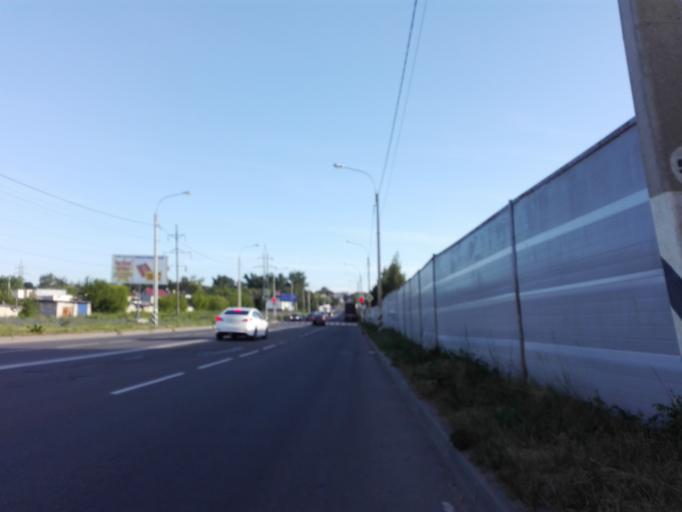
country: RU
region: Orjol
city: Orel
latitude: 52.9547
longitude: 36.0293
